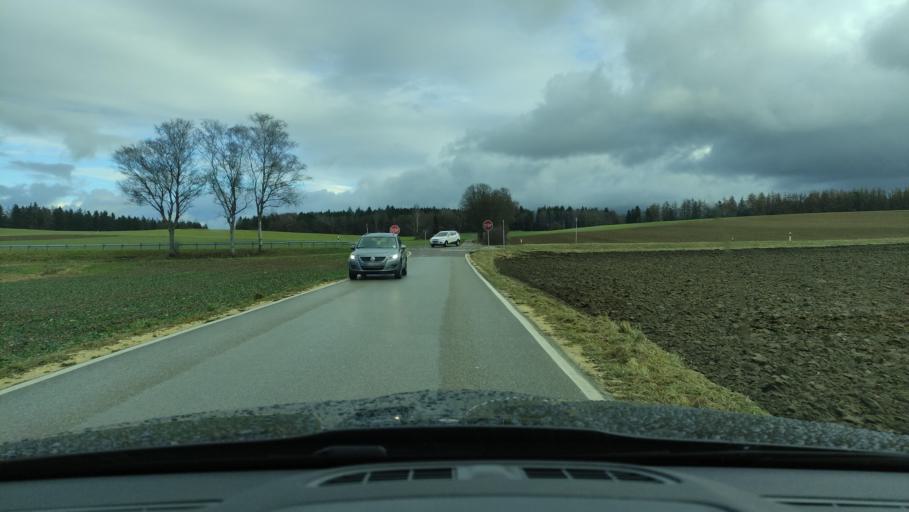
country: DE
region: Bavaria
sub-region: Swabia
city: Deisenhausen
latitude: 48.2769
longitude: 10.3368
